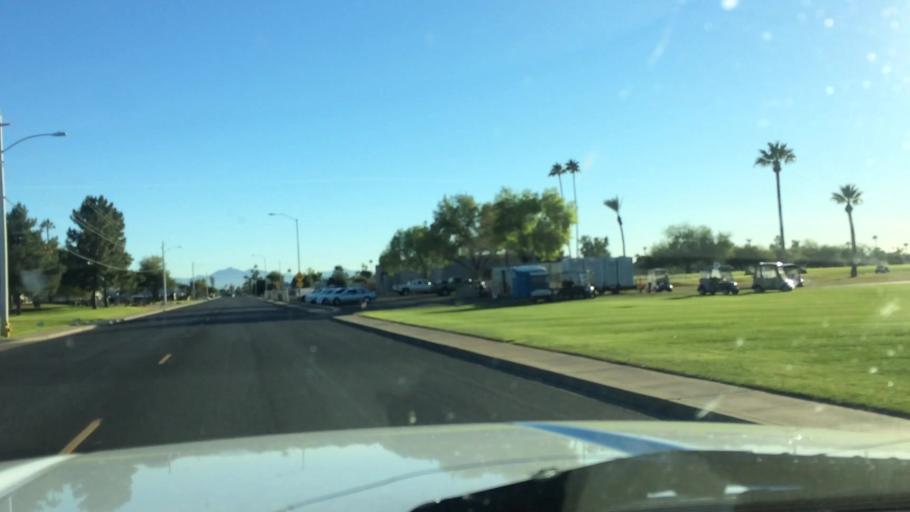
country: US
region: Arizona
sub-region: Maricopa County
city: Sun City
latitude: 33.5855
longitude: -112.2813
